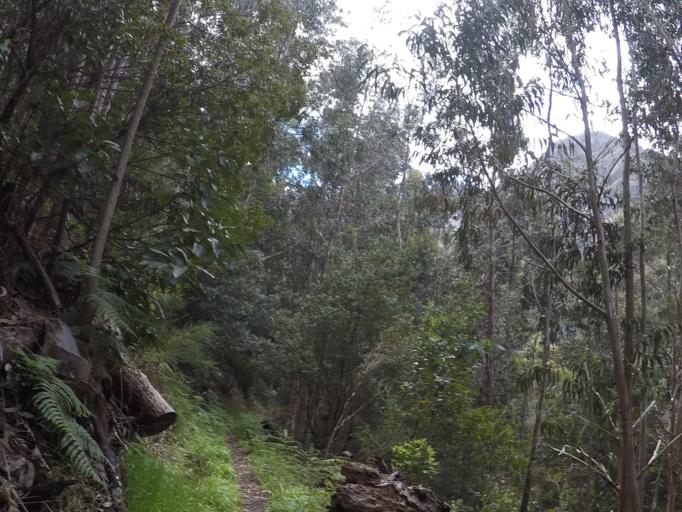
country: PT
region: Madeira
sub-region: Camara de Lobos
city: Curral das Freiras
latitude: 32.7471
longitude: -17.0045
